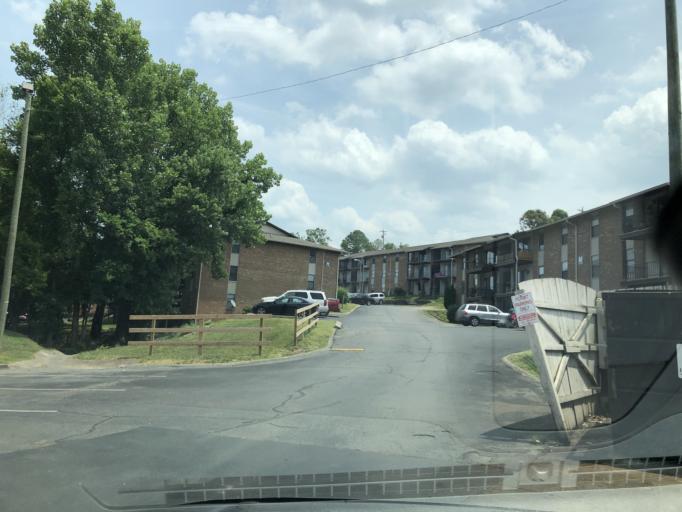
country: US
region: Tennessee
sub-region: Davidson County
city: Oak Hill
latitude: 36.0641
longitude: -86.6905
